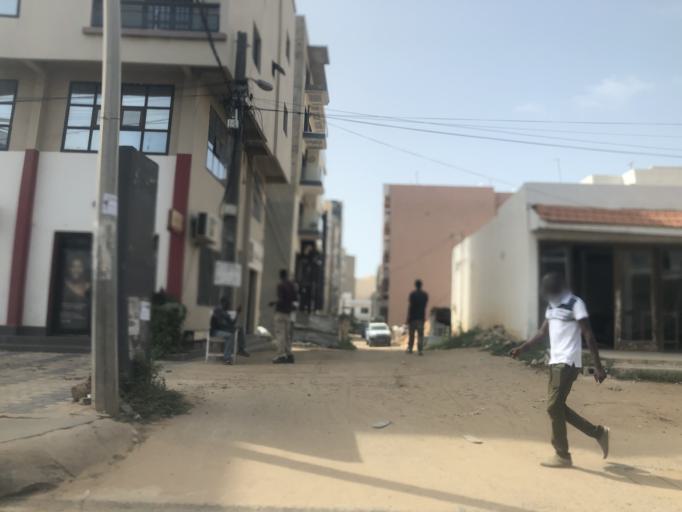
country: SN
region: Dakar
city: Mermoz Boabab
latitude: 14.7452
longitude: -17.5107
